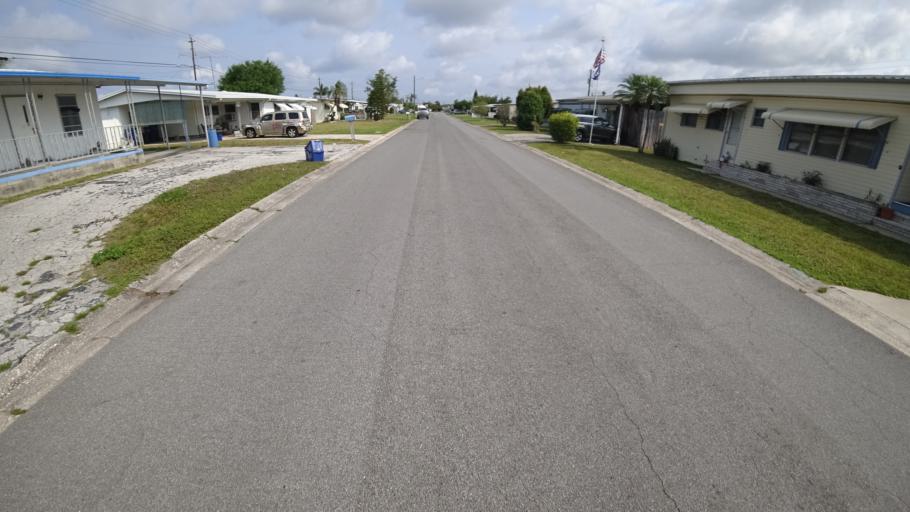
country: US
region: Florida
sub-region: Manatee County
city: South Bradenton
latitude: 27.4482
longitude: -82.5688
